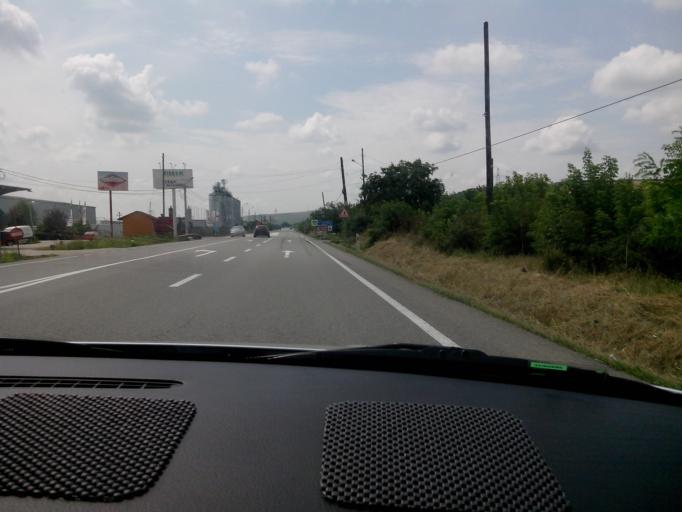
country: RO
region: Cluj
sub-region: Comuna Bontida
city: Rascruci
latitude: 46.9283
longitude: 23.7848
